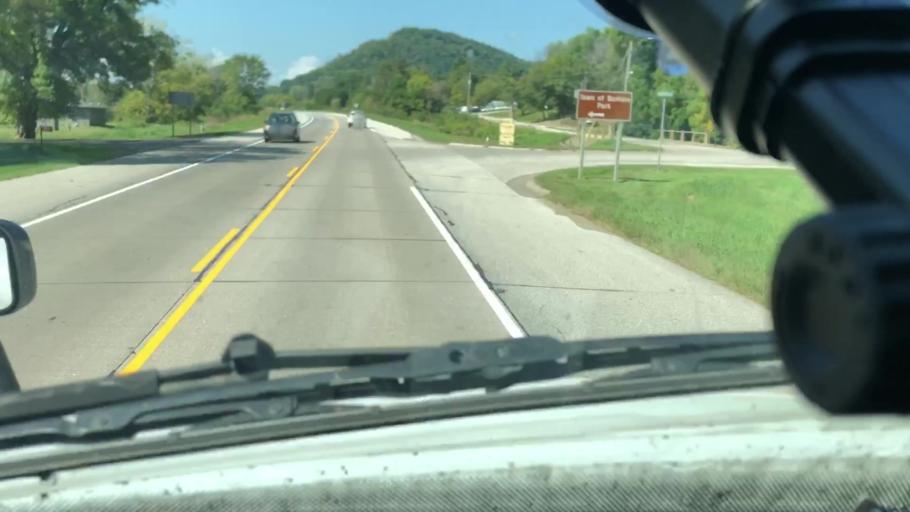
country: US
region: Minnesota
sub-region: Winona County
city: Winona
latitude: 44.0695
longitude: -91.6008
